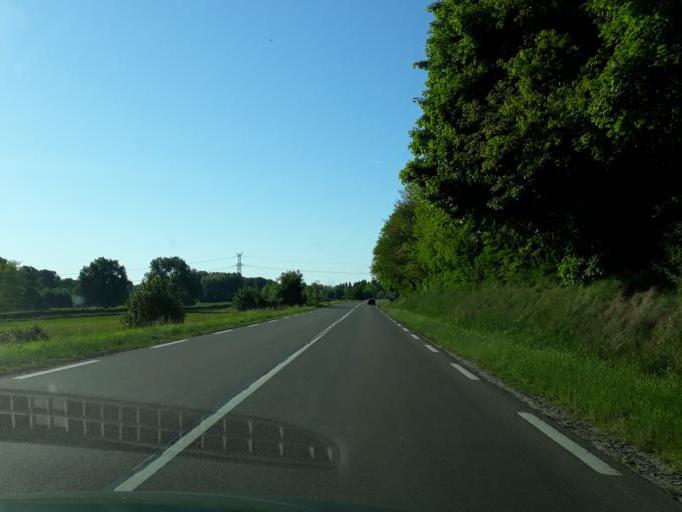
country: FR
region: Bourgogne
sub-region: Departement de la Nievre
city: Neuvy-sur-Loire
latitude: 47.5264
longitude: 2.8710
